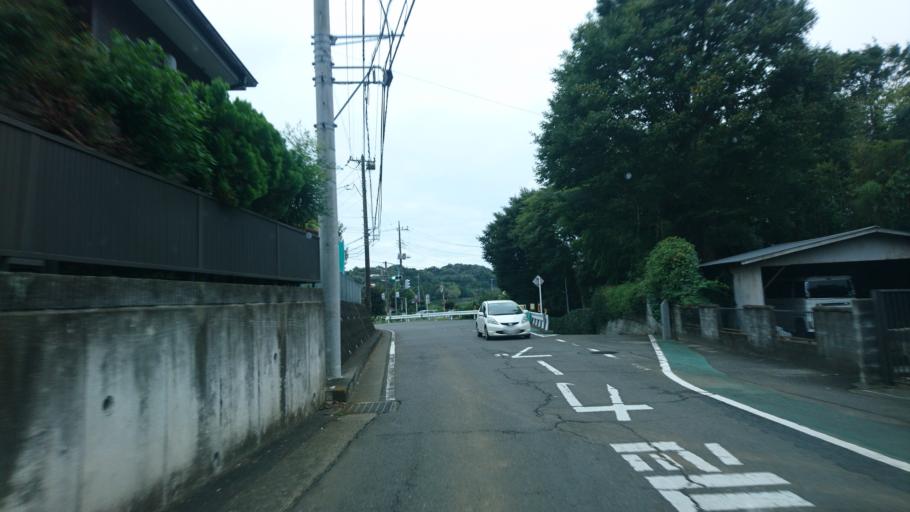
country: JP
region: Kanagawa
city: Atsugi
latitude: 35.4859
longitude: 139.3234
